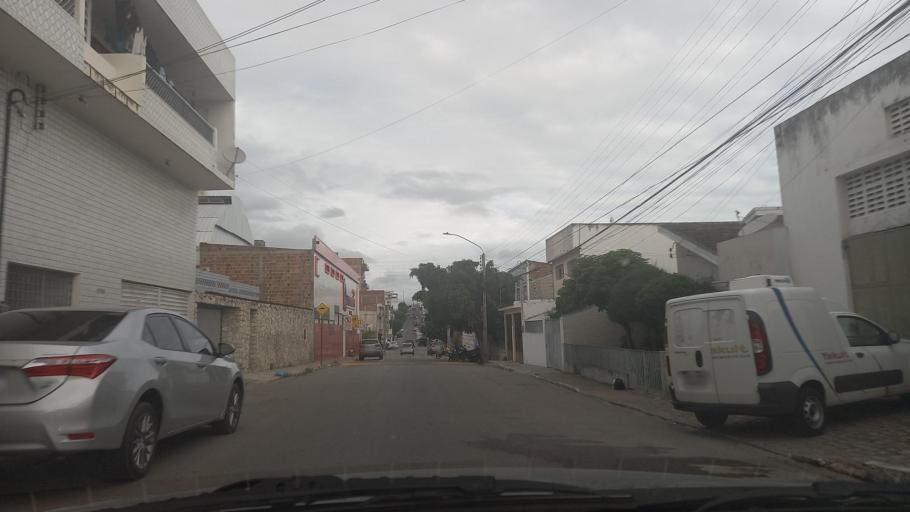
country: BR
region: Pernambuco
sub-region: Caruaru
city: Caruaru
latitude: -8.2765
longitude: -35.9812
